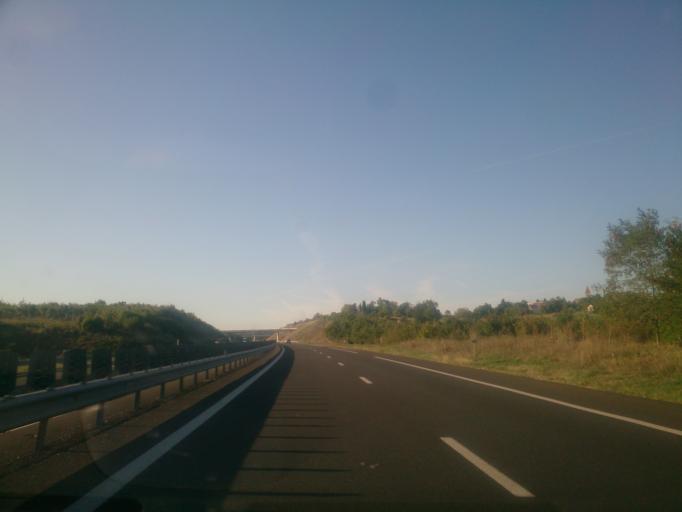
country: FR
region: Midi-Pyrenees
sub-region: Departement du Lot
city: Cahors
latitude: 44.5559
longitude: 1.5167
